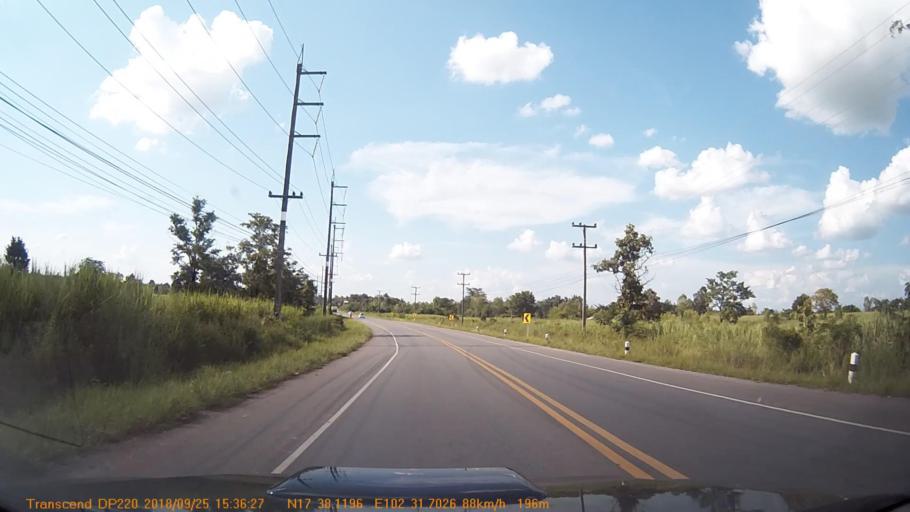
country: TH
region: Changwat Udon Thani
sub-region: Amphoe Ban Phue
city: Ban Phue
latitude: 17.6355
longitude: 102.5283
